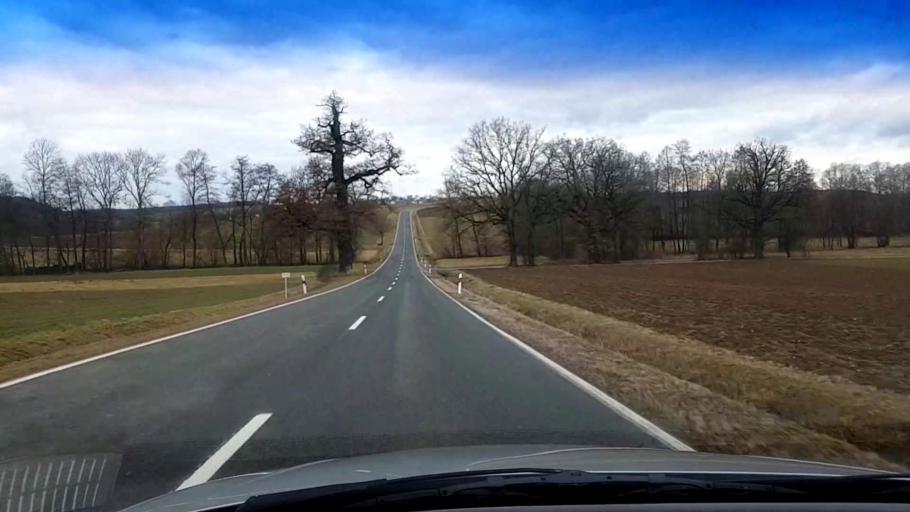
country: DE
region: Bavaria
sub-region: Upper Franconia
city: Schesslitz
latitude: 49.9860
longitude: 11.0133
